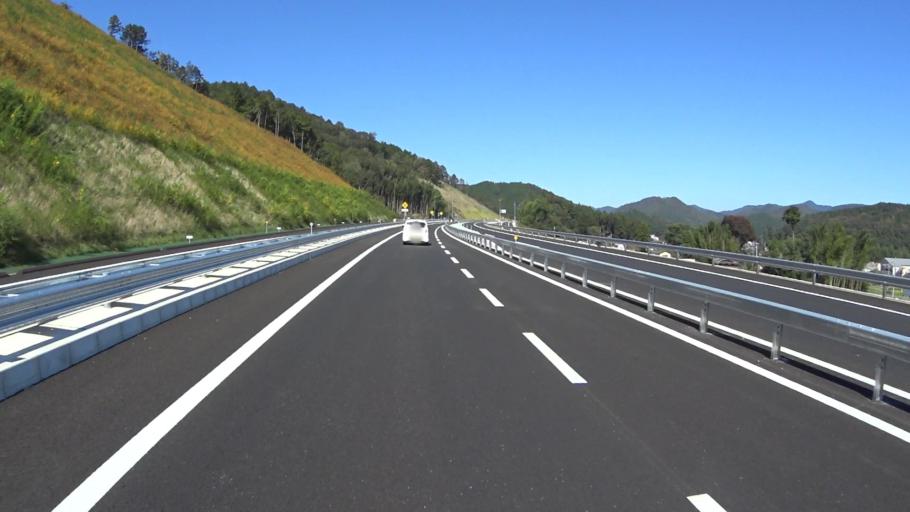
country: JP
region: Kyoto
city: Ayabe
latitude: 35.1846
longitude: 135.3623
